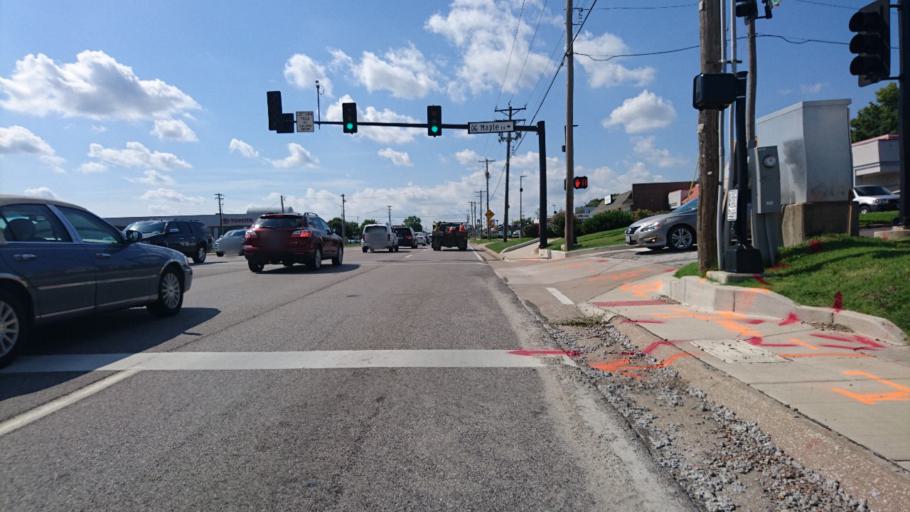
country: US
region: Missouri
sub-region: Saint Louis County
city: Winchester
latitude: 38.5931
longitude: -90.5298
